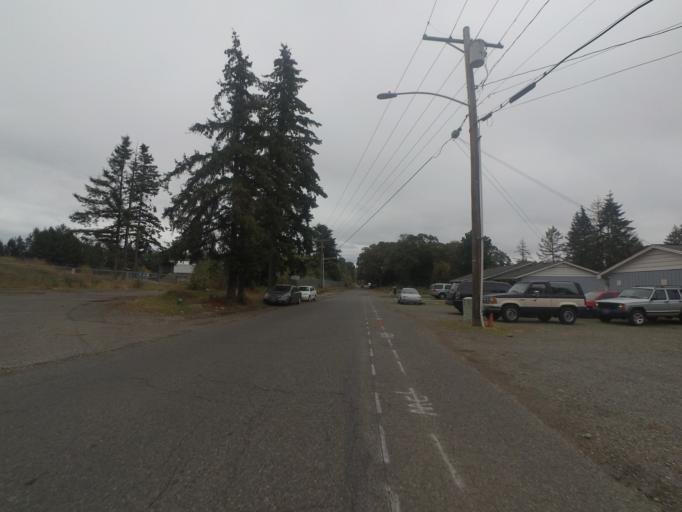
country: US
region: Washington
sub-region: Pierce County
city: McChord Air Force Base
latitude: 47.1483
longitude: -122.4992
